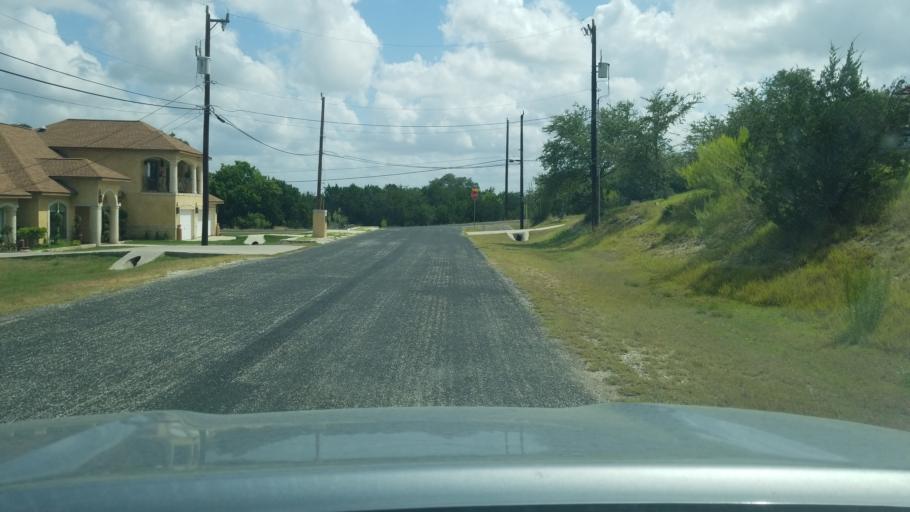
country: US
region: Texas
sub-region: Bexar County
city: Timberwood Park
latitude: 29.6840
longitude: -98.5134
